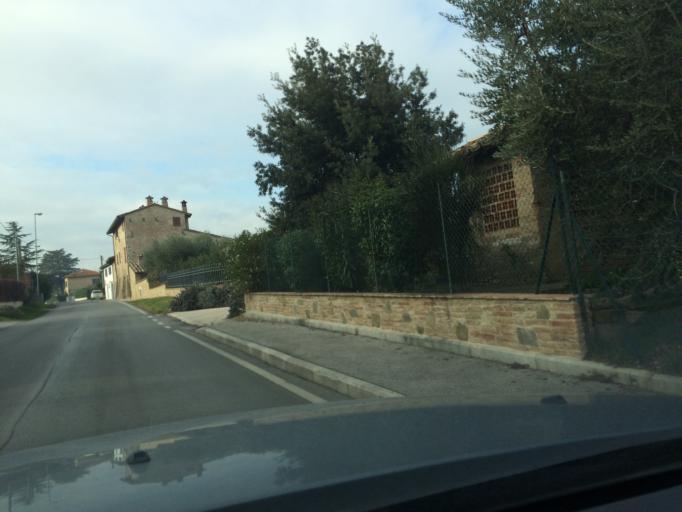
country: IT
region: Umbria
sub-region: Provincia di Perugia
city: Via Lippia
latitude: 43.0882
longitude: 12.4846
